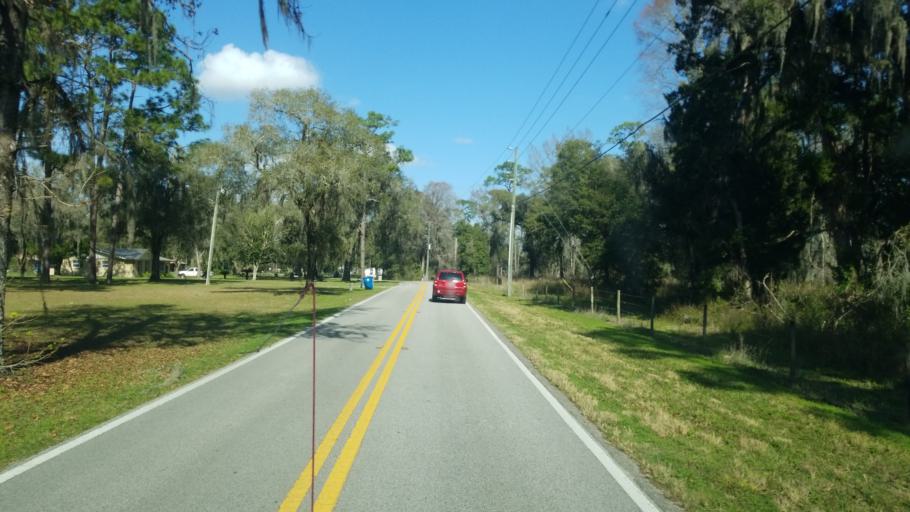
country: US
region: Florida
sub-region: Hernando County
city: North Brooksville
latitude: 28.5937
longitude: -82.3758
